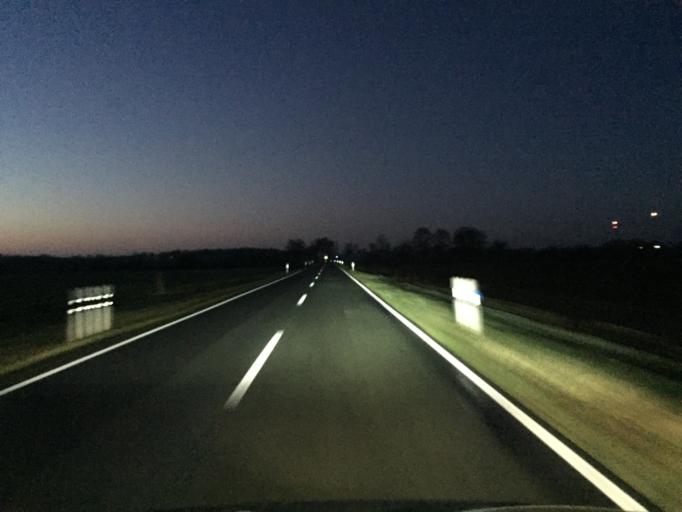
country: DE
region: Lower Saxony
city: Maasen
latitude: 52.6565
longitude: 8.8864
